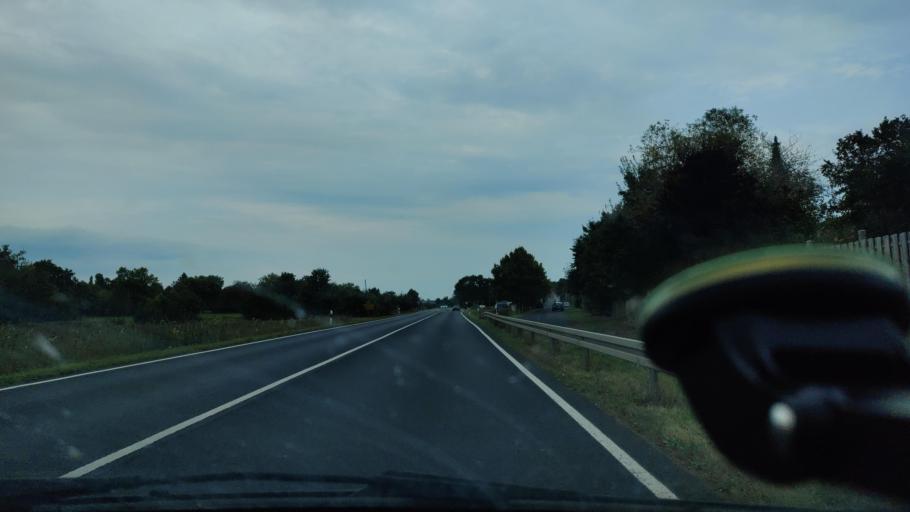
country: DE
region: Bavaria
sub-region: Regierungsbezirk Unterfranken
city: Sulzfeld am Main
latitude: 49.7157
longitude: 10.1504
